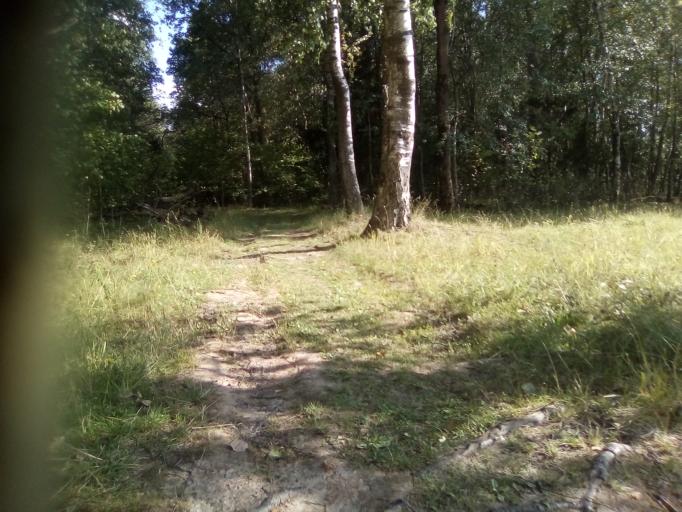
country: RU
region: Moskovskaya
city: Kokoshkino
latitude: 55.6158
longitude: 37.1746
